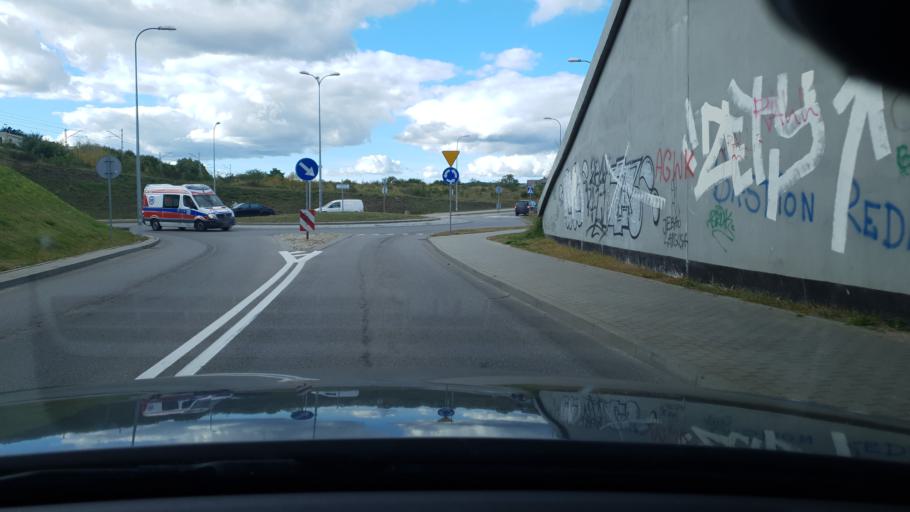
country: PL
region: Pomeranian Voivodeship
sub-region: Powiat wejherowski
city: Reda
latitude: 54.6015
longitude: 18.3458
